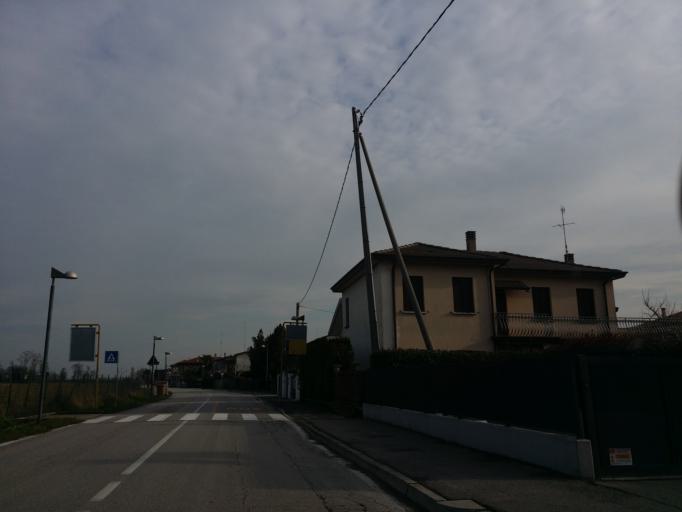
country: IT
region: Veneto
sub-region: Provincia di Padova
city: Terradura
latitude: 45.3501
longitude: 11.8198
